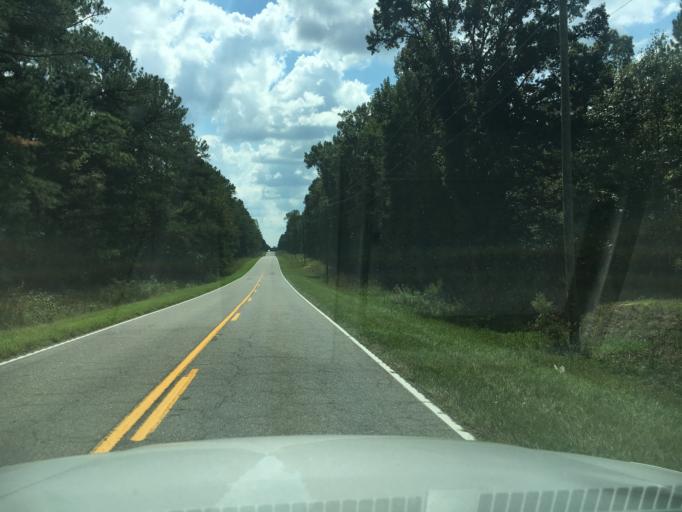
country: US
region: South Carolina
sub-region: Greenwood County
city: Greenwood
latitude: 34.0981
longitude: -82.1289
